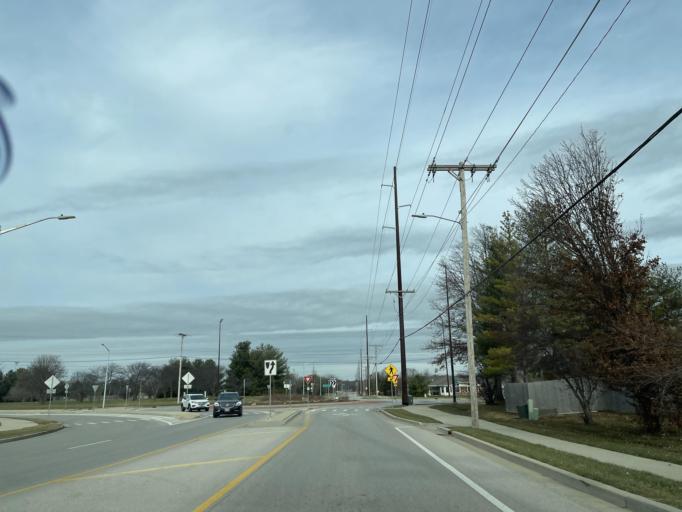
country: US
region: Illinois
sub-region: Sangamon County
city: Jerome
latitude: 39.7702
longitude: -89.7346
